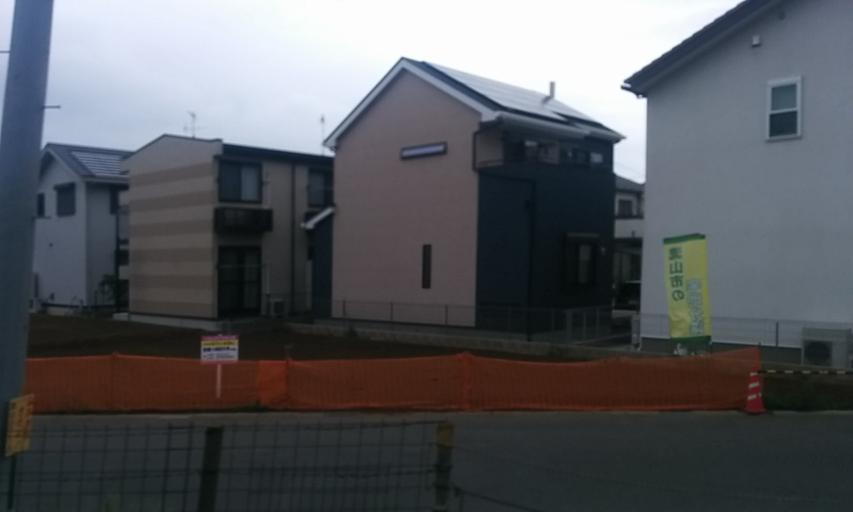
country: JP
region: Chiba
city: Nagareyama
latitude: 35.8469
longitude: 139.9041
